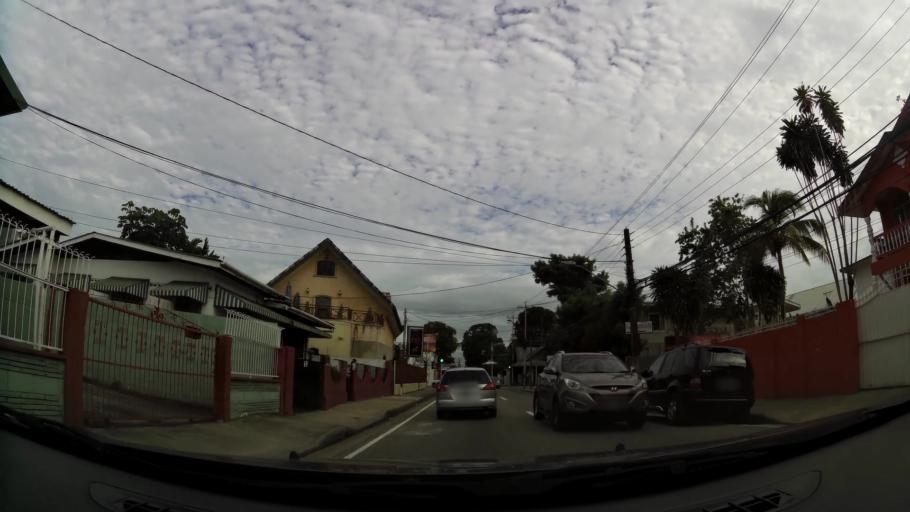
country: TT
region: City of Port of Spain
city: Port-of-Spain
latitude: 10.6644
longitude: -61.5228
